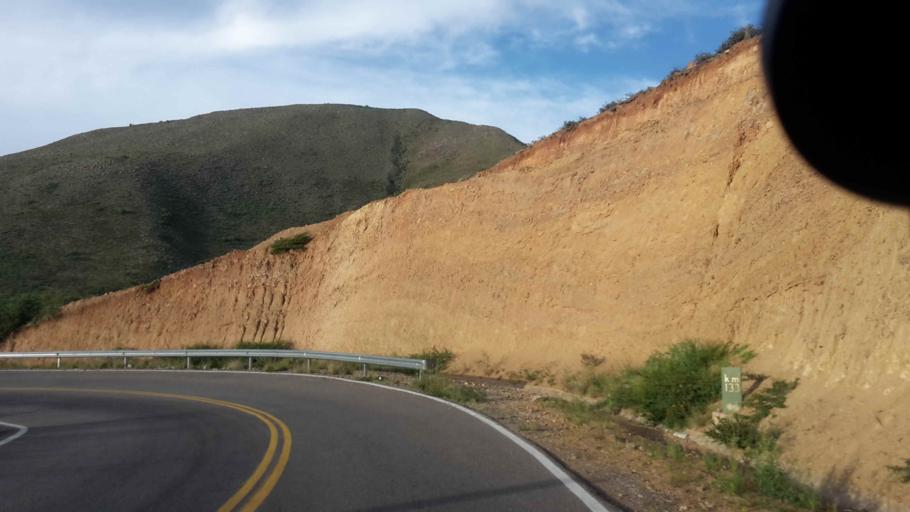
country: BO
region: Cochabamba
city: Arani
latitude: -17.5772
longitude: -65.7526
